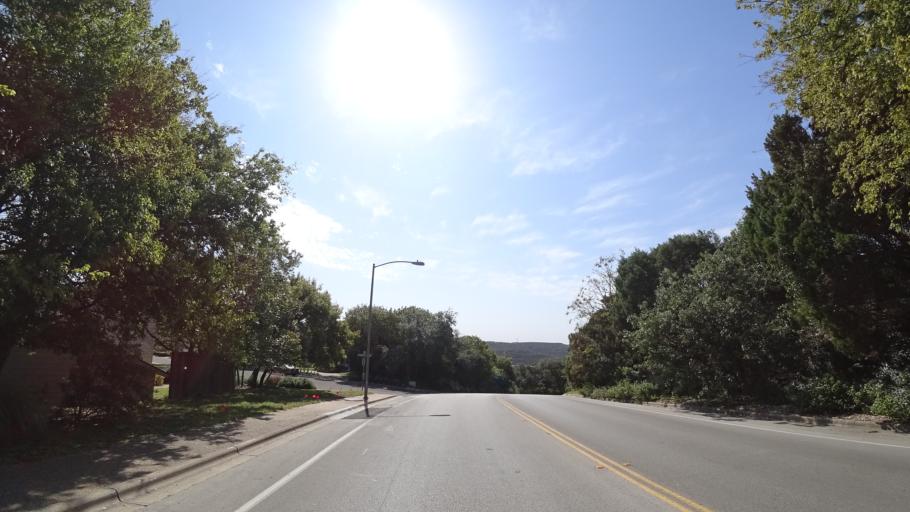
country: US
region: Texas
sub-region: Travis County
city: West Lake Hills
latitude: 30.3504
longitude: -97.7716
